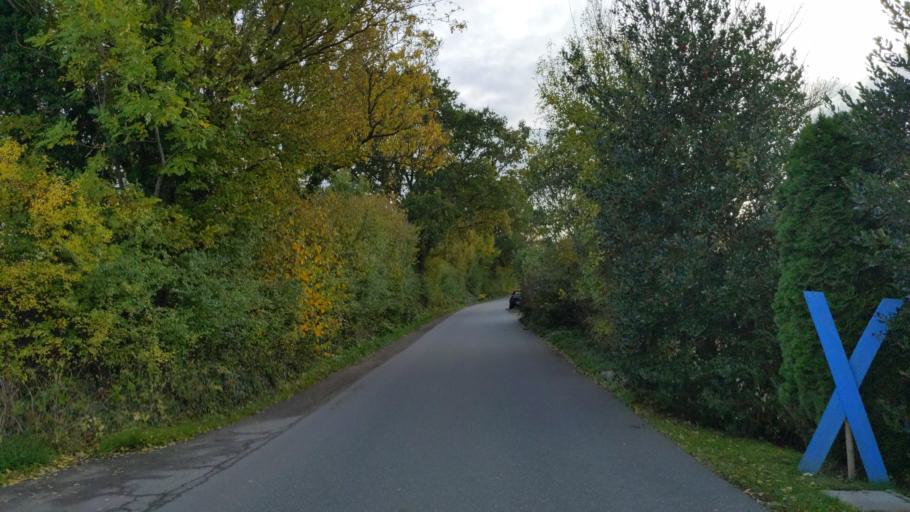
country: DE
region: Schleswig-Holstein
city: Susel
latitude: 54.0661
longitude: 10.7330
